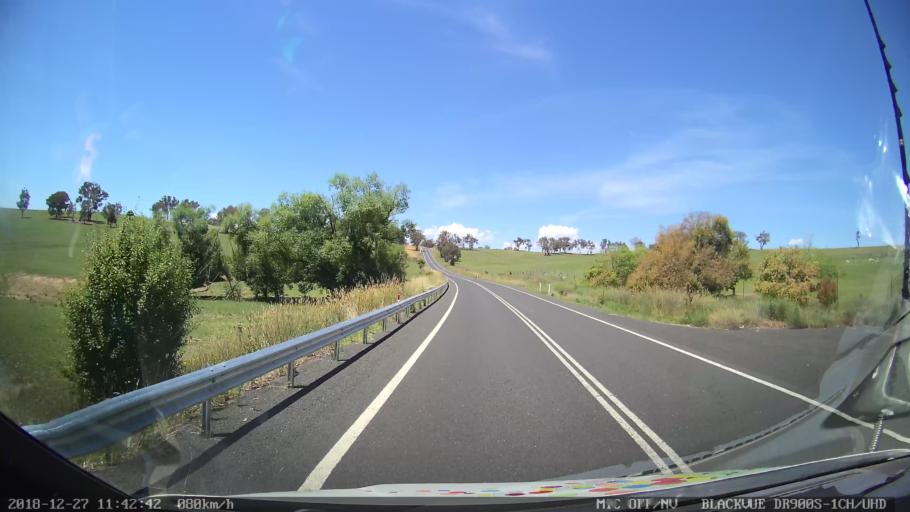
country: AU
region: New South Wales
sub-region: Bathurst Regional
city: Perthville
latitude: -33.5517
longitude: 149.4776
